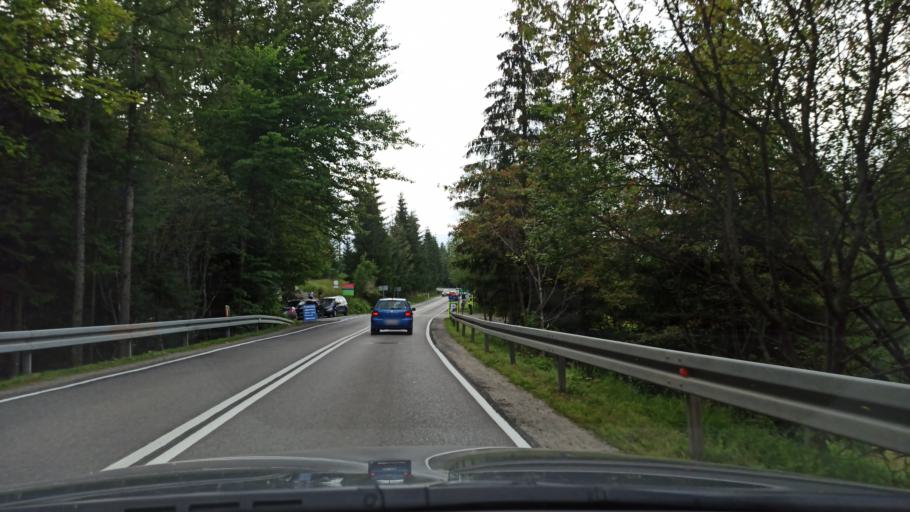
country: PL
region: Lesser Poland Voivodeship
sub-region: Powiat tatrzanski
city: Koscielisko
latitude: 49.2782
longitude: 19.9051
